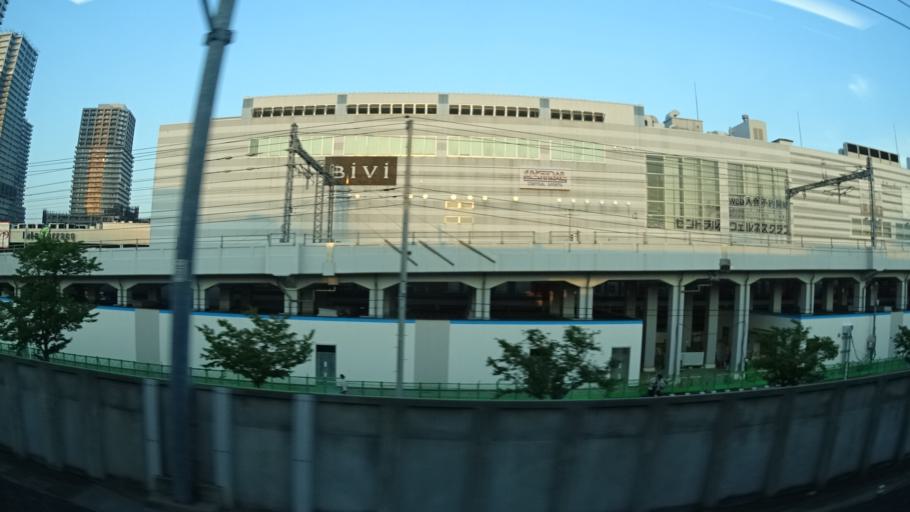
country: JP
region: Saitama
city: Soka
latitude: 35.7352
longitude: 139.8001
